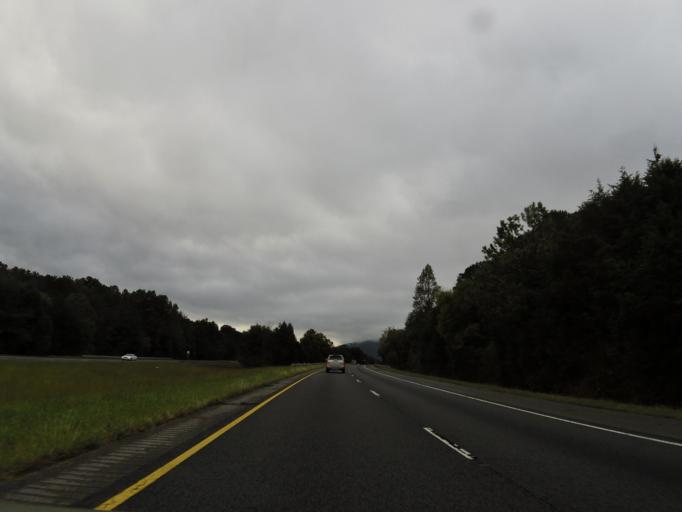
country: US
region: Georgia
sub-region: Dade County
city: Trenton
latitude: 34.9527
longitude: -85.4646
